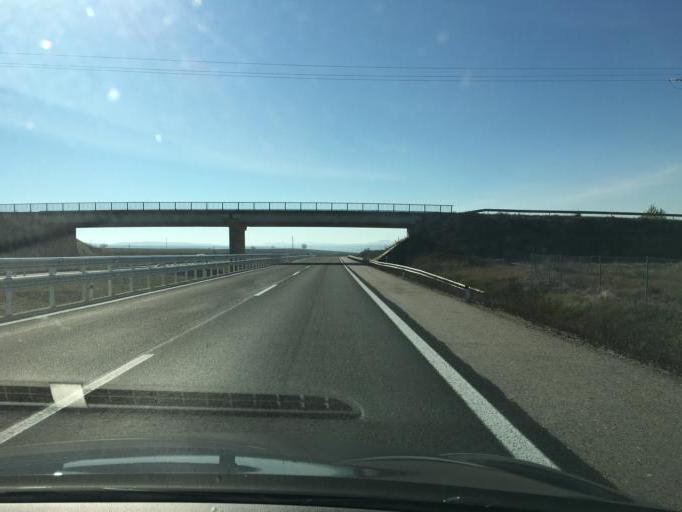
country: ES
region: Castille and Leon
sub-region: Provincia de Burgos
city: Briviesca
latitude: 42.5508
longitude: -3.2854
